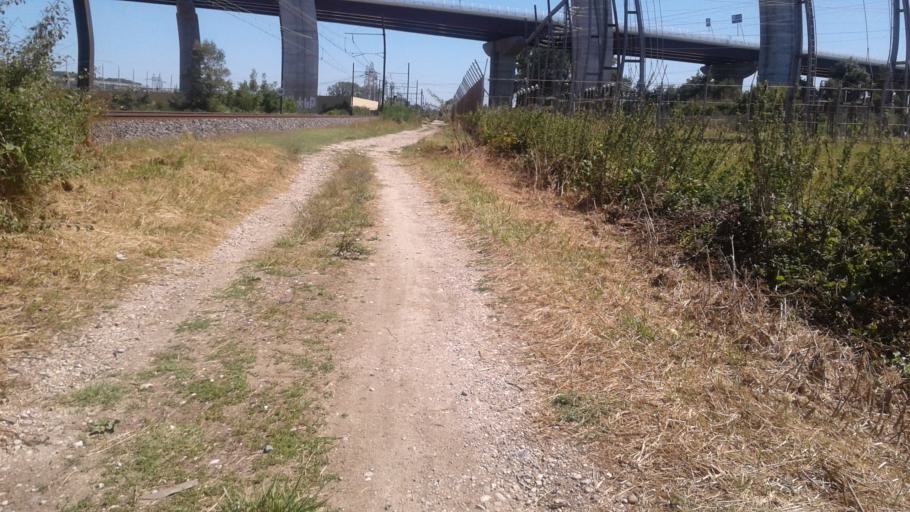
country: FR
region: Rhone-Alpes
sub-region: Departement de l'Ain
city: Beynost
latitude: 45.8361
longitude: 5.0177
